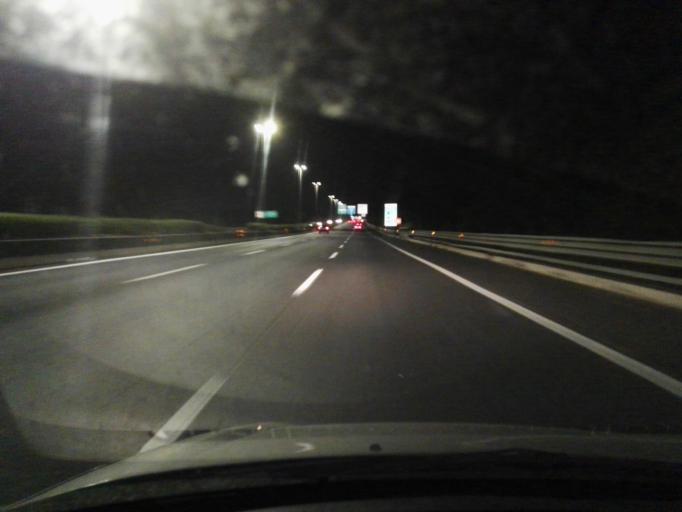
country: IT
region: Latium
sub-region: Citta metropolitana di Roma Capitale
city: Selcetta
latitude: 41.7996
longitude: 12.4648
